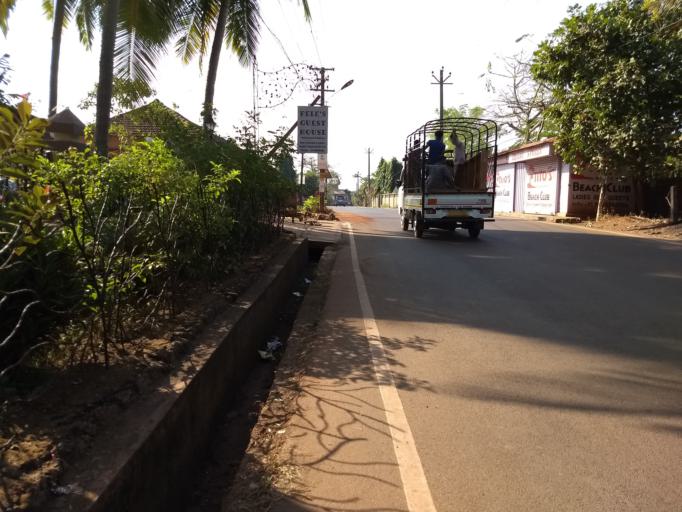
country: IN
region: Goa
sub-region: North Goa
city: Vagator
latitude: 15.5938
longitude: 73.7442
